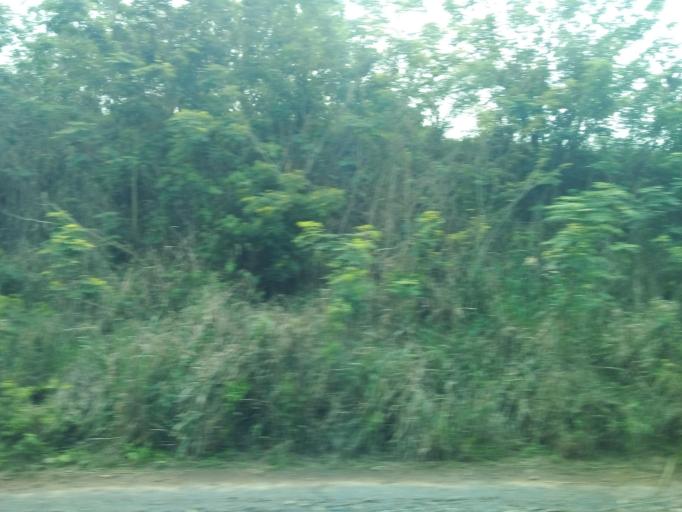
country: BR
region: Minas Gerais
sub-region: Governador Valadares
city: Governador Valadares
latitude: -19.0894
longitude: -42.1633
